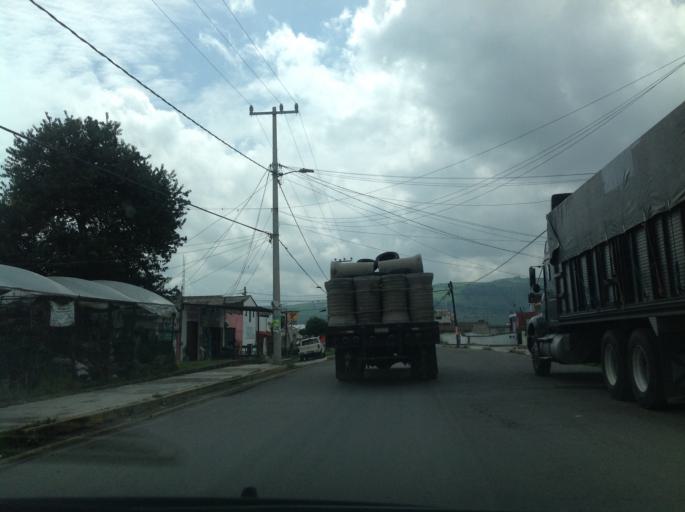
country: MX
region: Morelos
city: Tenango de Arista
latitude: 19.1034
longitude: -99.5846
